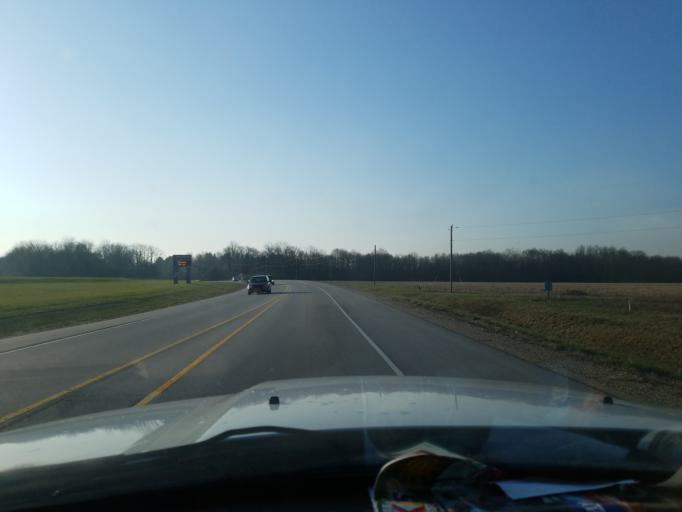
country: US
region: Indiana
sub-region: Vigo County
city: Terre Haute
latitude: 39.4101
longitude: -87.3316
